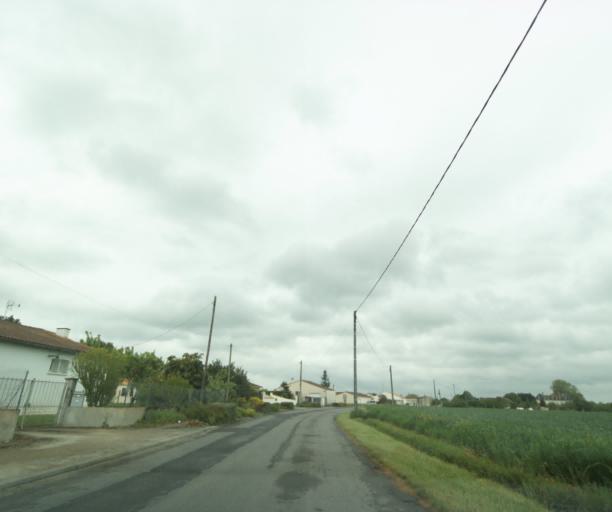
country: FR
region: Poitou-Charentes
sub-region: Departement de la Charente-Maritime
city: Chaniers
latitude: 45.6967
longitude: -0.5173
